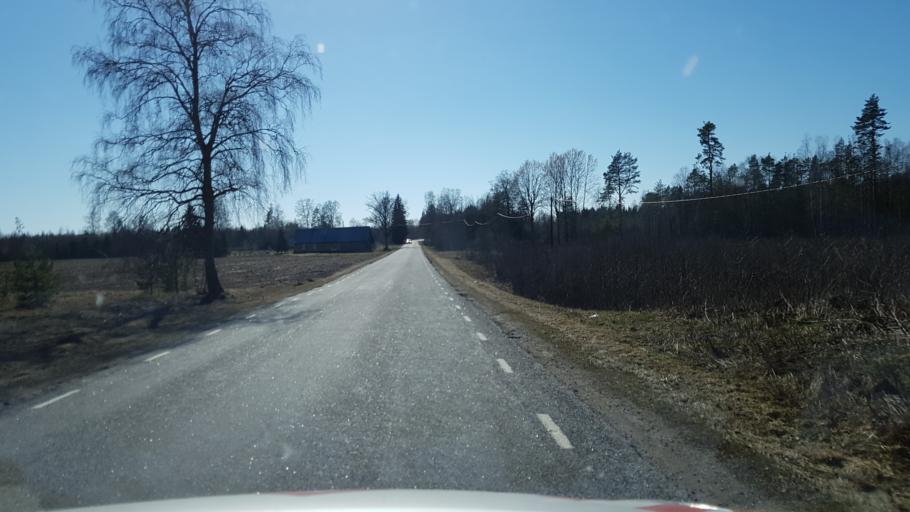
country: EE
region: Laeaene-Virumaa
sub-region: Tamsalu vald
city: Tamsalu
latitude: 59.0806
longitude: 26.1519
